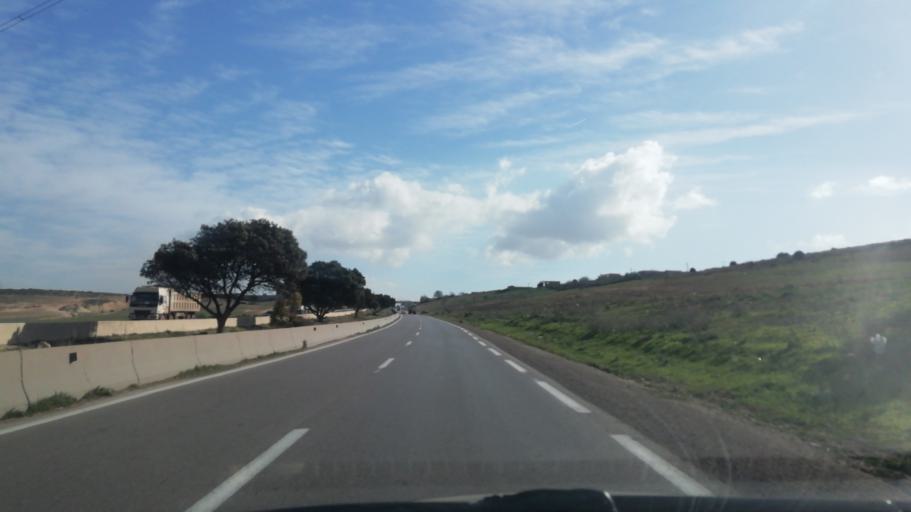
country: DZ
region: Oran
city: Ain el Bya
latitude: 35.7677
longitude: -0.2298
